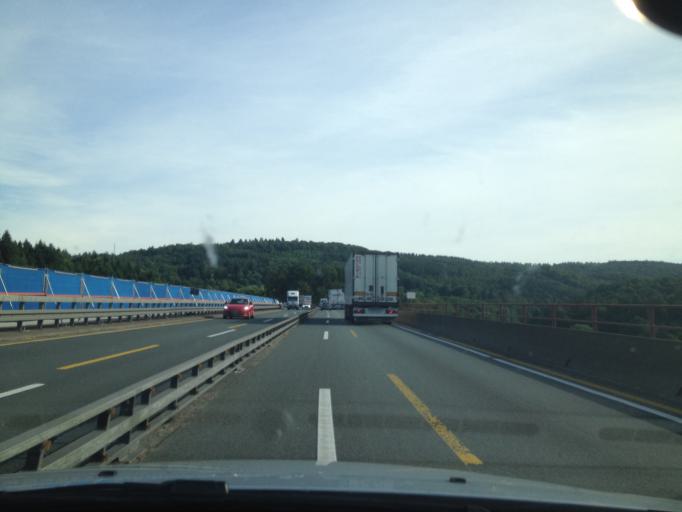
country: DE
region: Hesse
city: Dillenburg
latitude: 50.7360
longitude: 8.2740
